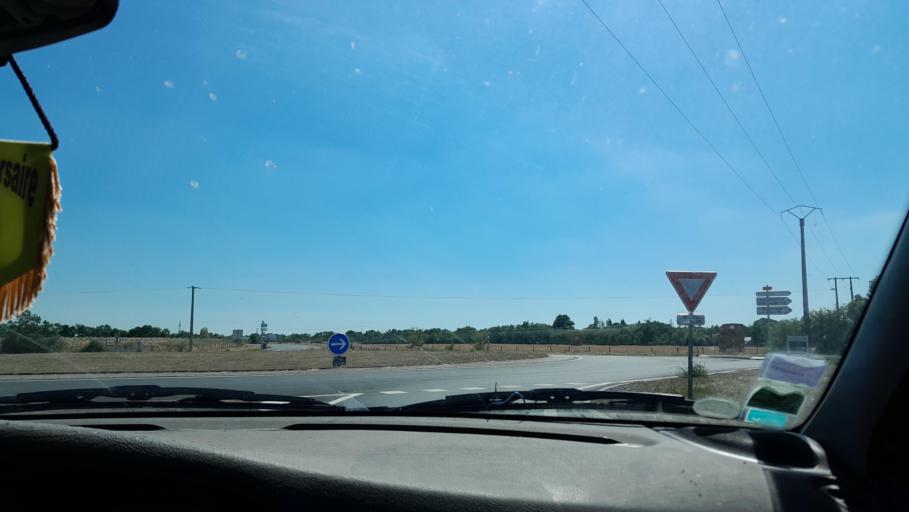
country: FR
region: Pays de la Loire
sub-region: Departement de la Loire-Atlantique
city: Saint-Gereon
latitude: 47.3805
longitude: -1.2101
